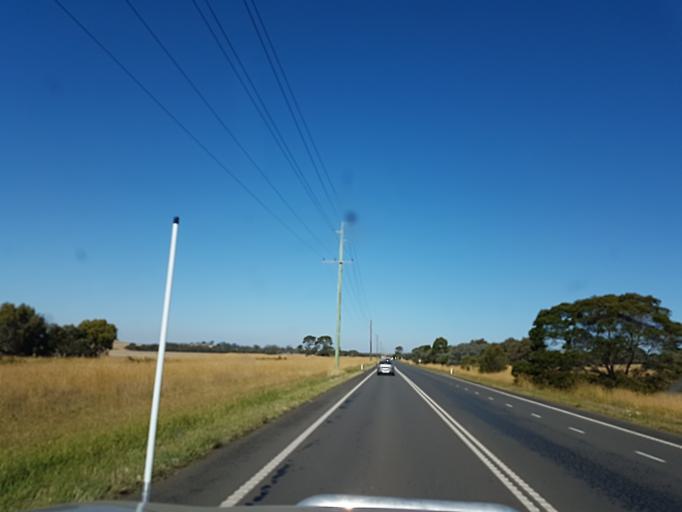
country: AU
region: Victoria
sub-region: Colac-Otway
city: Colac
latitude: -38.3119
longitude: 143.7032
